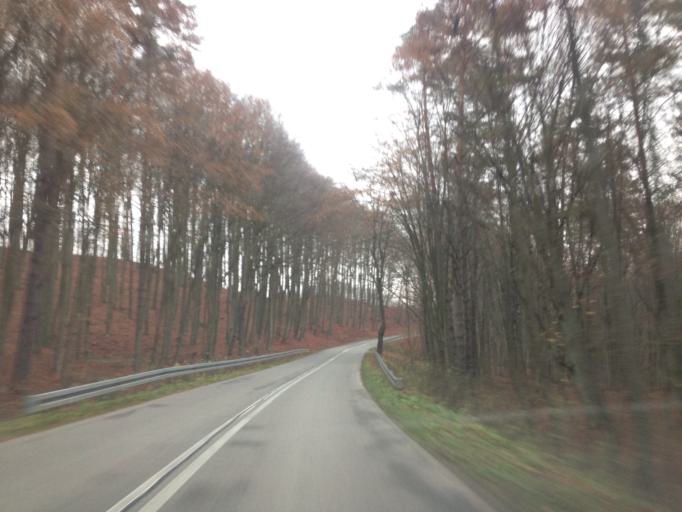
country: PL
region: Pomeranian Voivodeship
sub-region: Powiat gdanski
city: Przywidz
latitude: 54.1860
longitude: 18.3447
